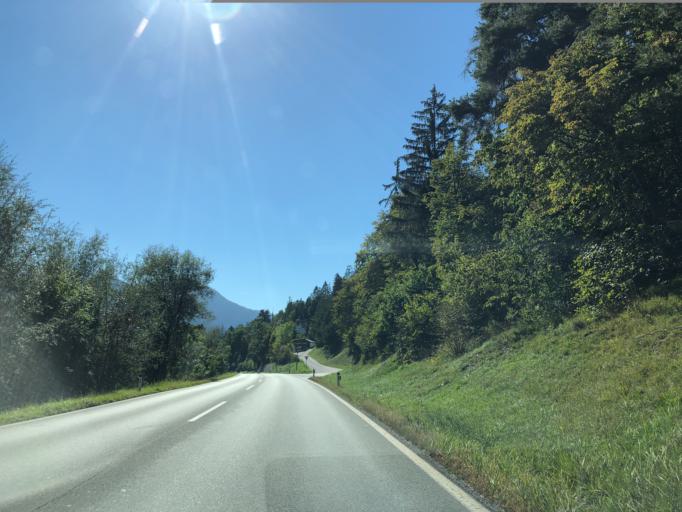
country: AT
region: Tyrol
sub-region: Politischer Bezirk Imst
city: Imst
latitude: 47.2526
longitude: 10.7481
